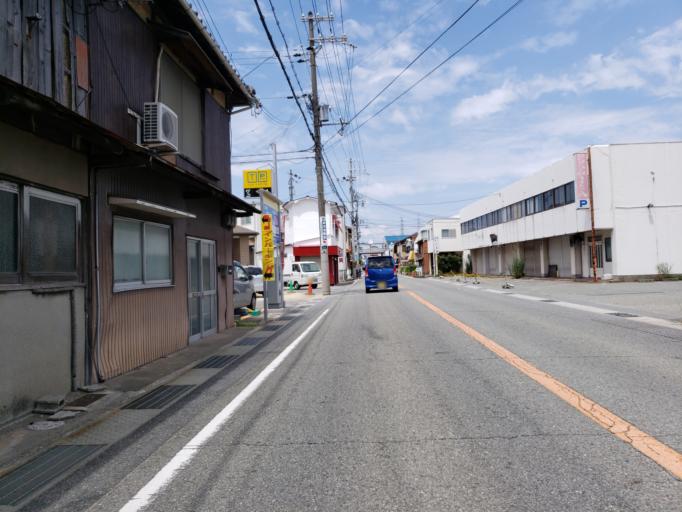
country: JP
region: Hyogo
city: Shirahamacho-usazakiminami
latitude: 34.7864
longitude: 134.7095
